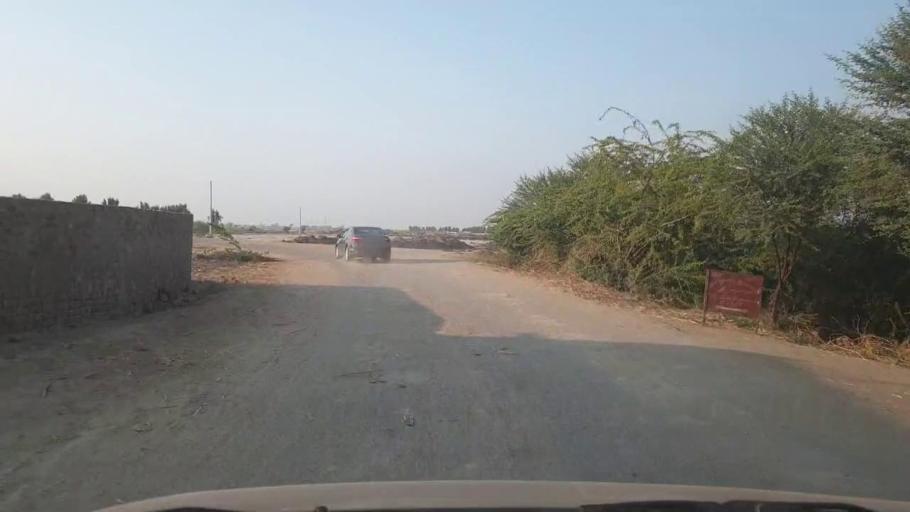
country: PK
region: Sindh
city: Mirwah Gorchani
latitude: 25.3678
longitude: 69.1779
